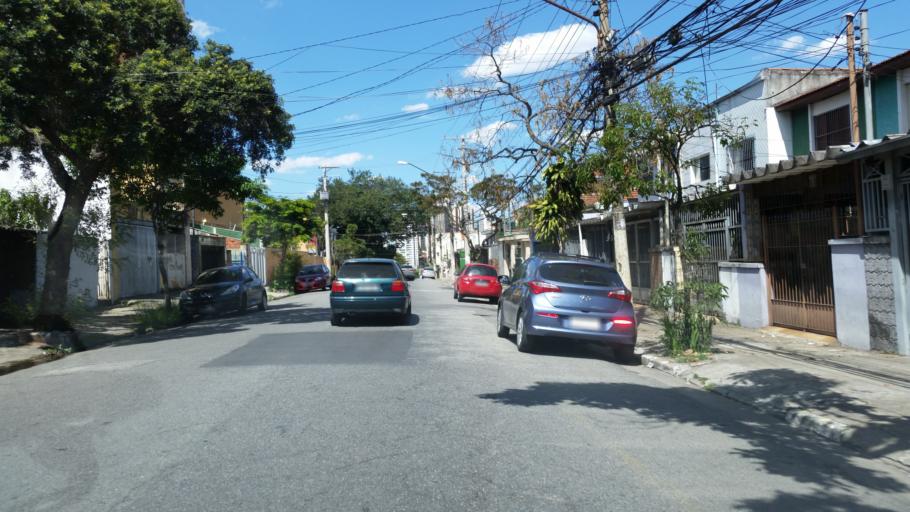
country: BR
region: Sao Paulo
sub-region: Diadema
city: Diadema
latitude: -23.6231
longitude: -46.6341
